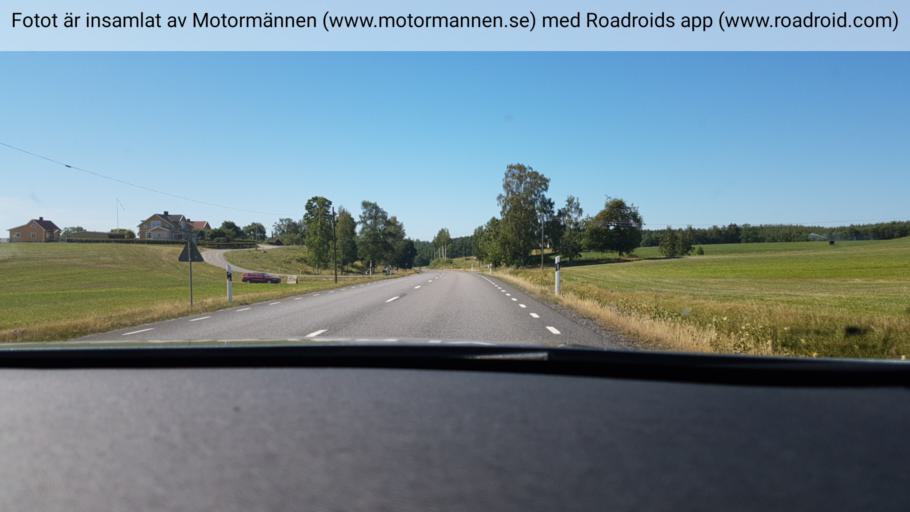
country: SE
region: Joenkoeping
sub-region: Habo Kommun
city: Habo
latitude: 57.9875
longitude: 14.1107
